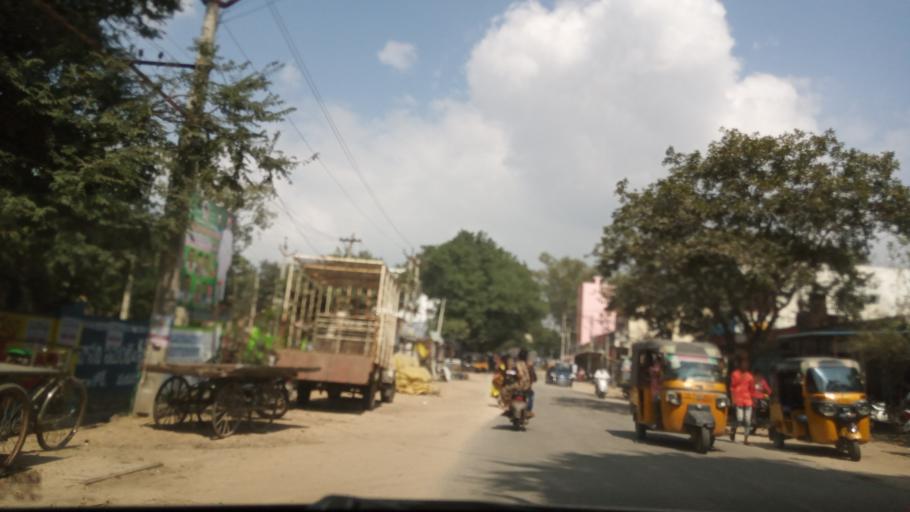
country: IN
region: Andhra Pradesh
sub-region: Chittoor
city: Madanapalle
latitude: 13.5624
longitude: 78.5112
